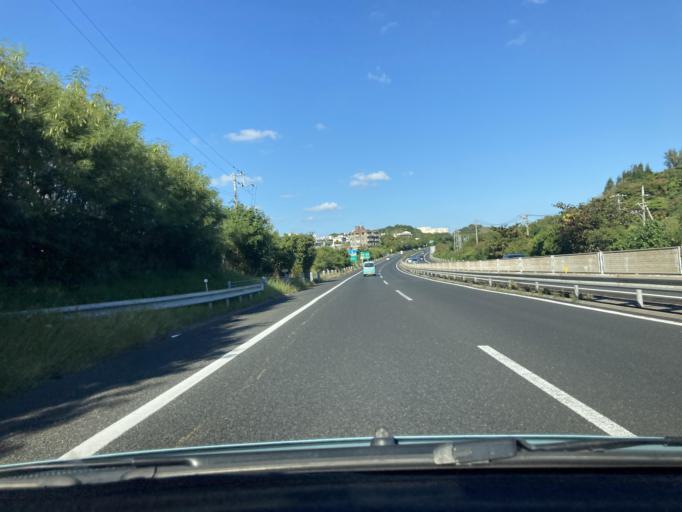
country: JP
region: Okinawa
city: Ginowan
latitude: 26.2423
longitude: 127.7437
